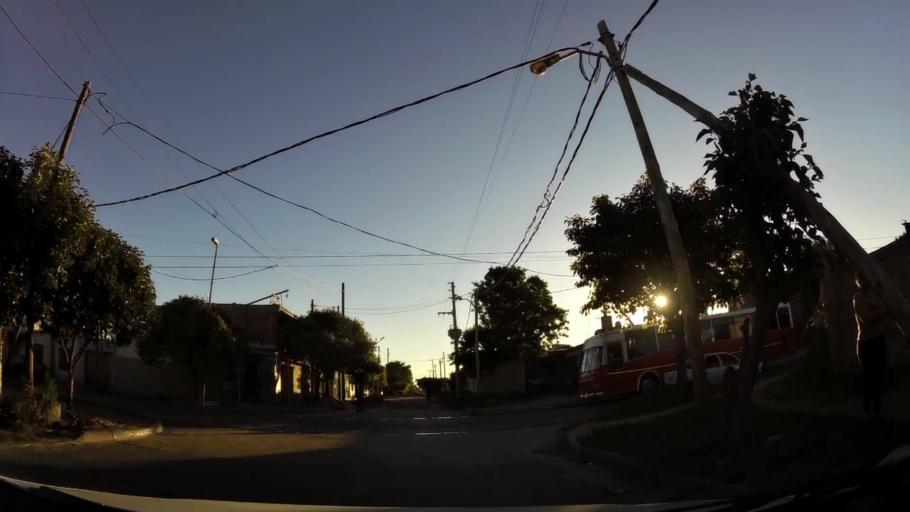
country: AR
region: Buenos Aires
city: San Justo
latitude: -34.7233
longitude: -58.6094
